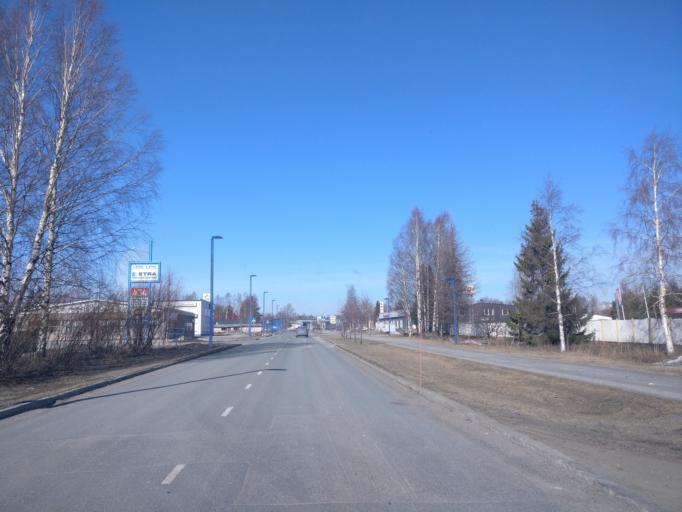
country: FI
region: Lapland
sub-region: Kemi-Tornio
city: Kemi
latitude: 65.7379
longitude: 24.5796
